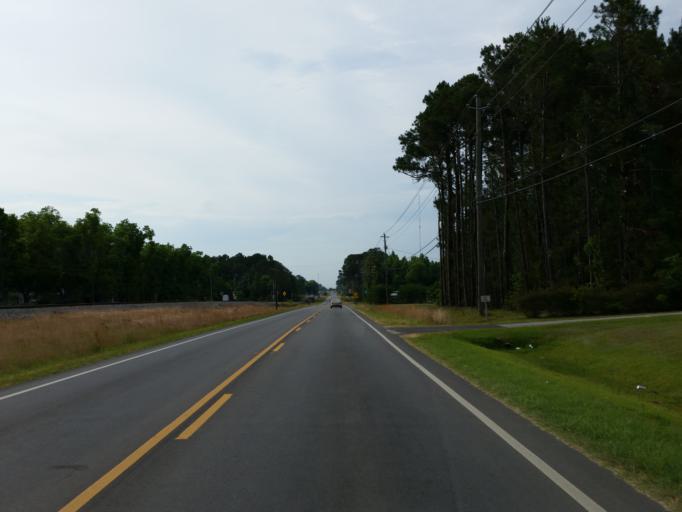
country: US
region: Georgia
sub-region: Turner County
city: Ashburn
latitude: 31.6828
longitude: -83.6418
